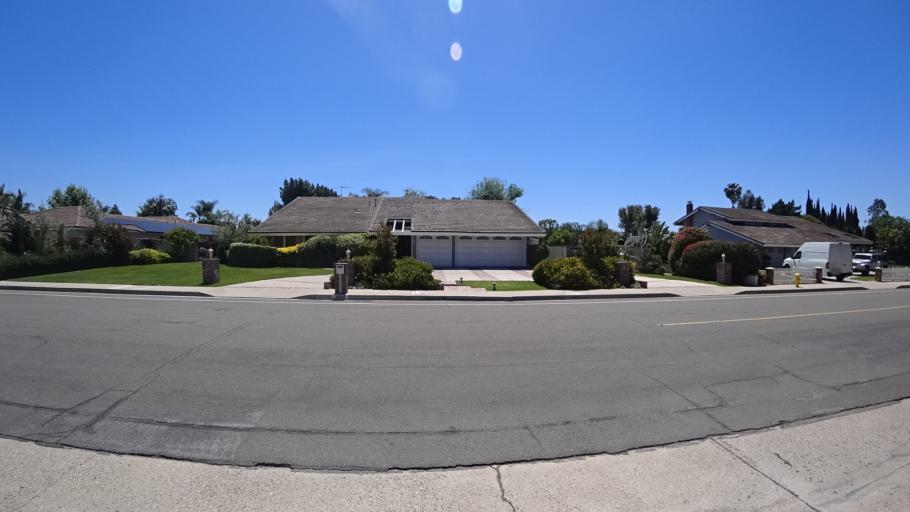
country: US
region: California
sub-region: Orange County
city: Villa Park
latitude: 33.8079
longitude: -117.8168
